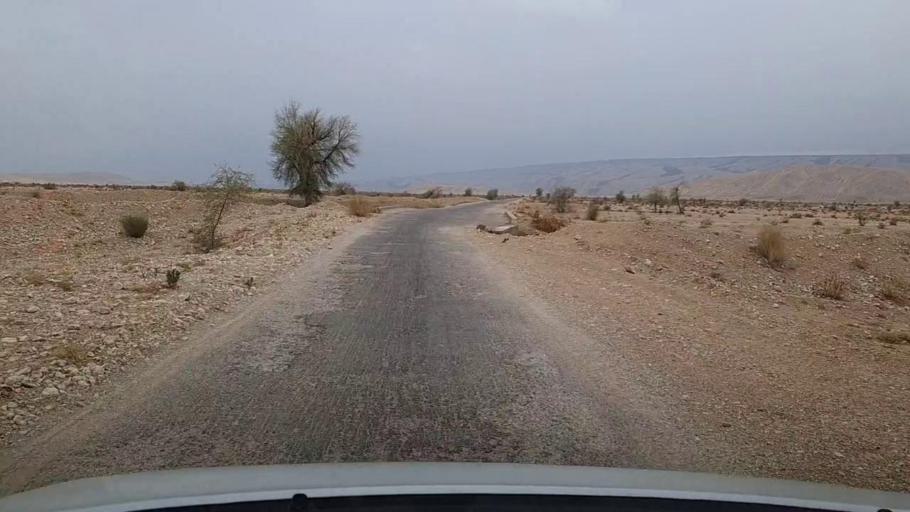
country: PK
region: Sindh
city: Sehwan
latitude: 26.2573
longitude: 67.7215
